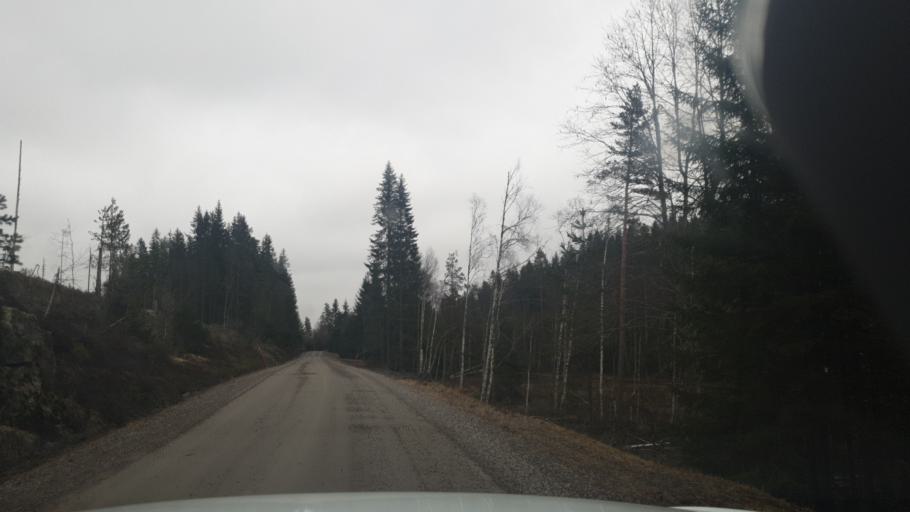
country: NO
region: Ostfold
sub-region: Romskog
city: Romskog
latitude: 59.7094
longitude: 12.0385
